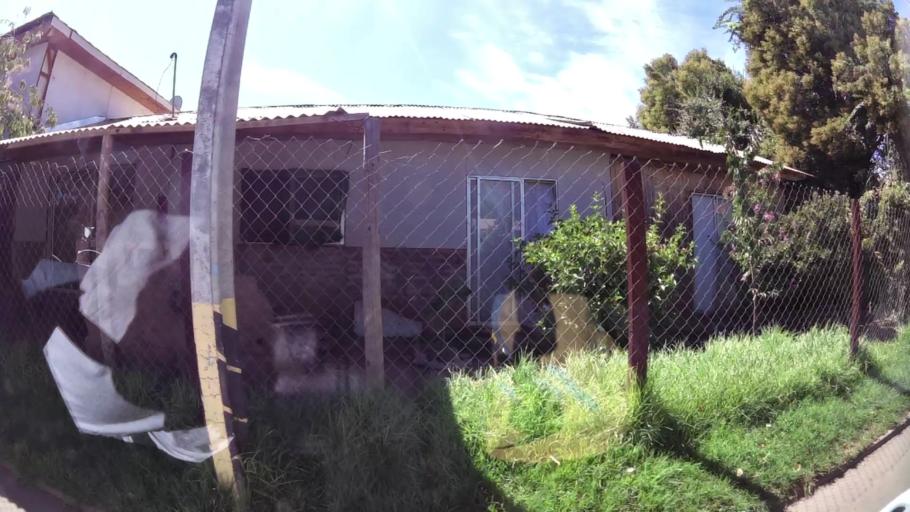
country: CL
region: O'Higgins
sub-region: Provincia de Cachapoal
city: Graneros
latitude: -33.9723
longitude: -70.7138
